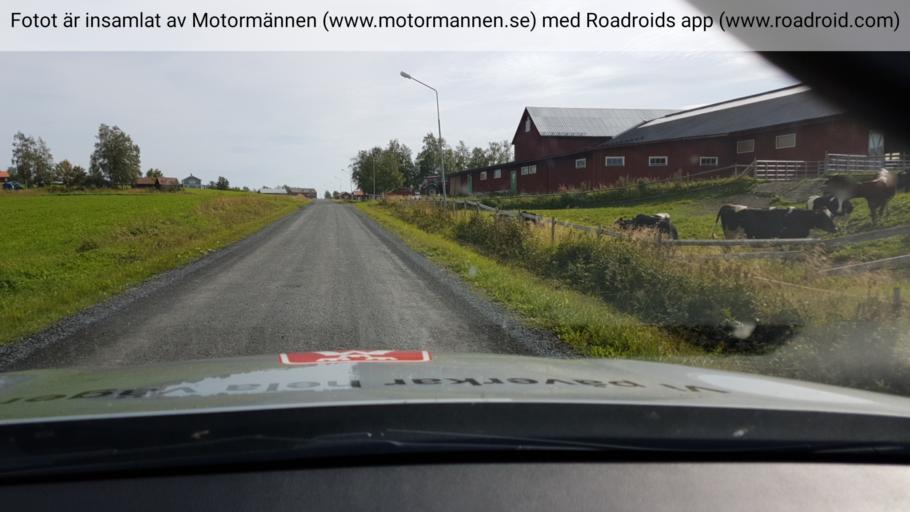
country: SE
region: Jaemtland
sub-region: Krokoms Kommun
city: Valla
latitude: 63.3565
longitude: 13.9741
